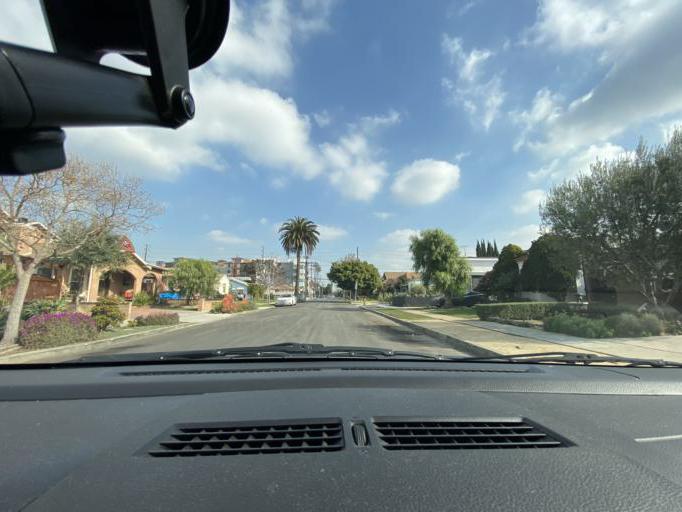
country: US
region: California
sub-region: Los Angeles County
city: Culver City
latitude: 34.0227
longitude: -118.4116
